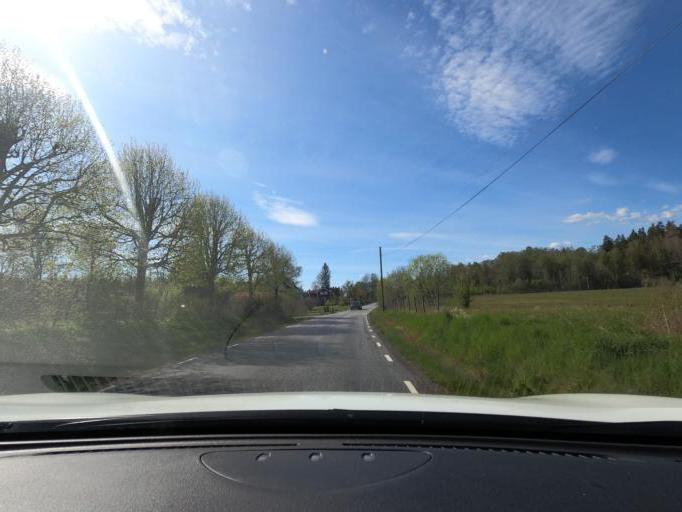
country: SE
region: Vaestra Goetaland
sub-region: Marks Kommun
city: Kinna
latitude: 57.4756
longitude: 12.5753
